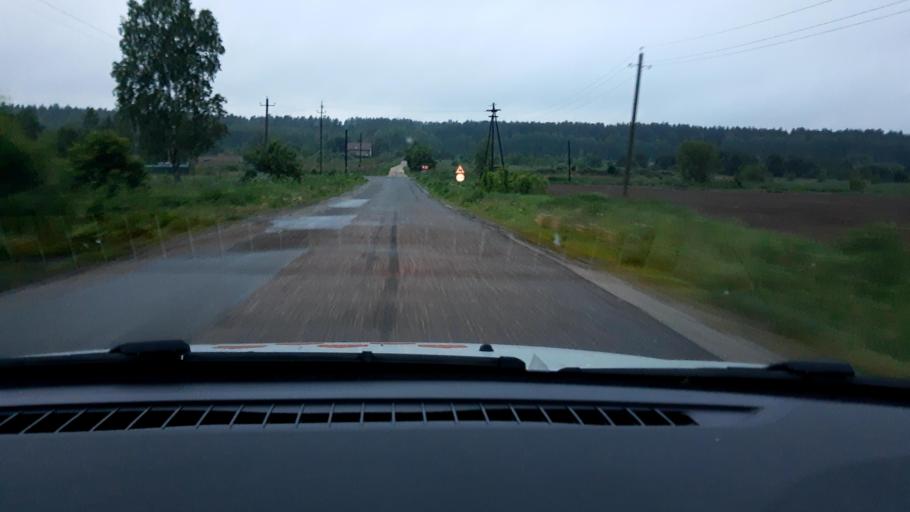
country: RU
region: Nizjnij Novgorod
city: Novaya Balakhna
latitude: 56.6337
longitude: 43.6192
